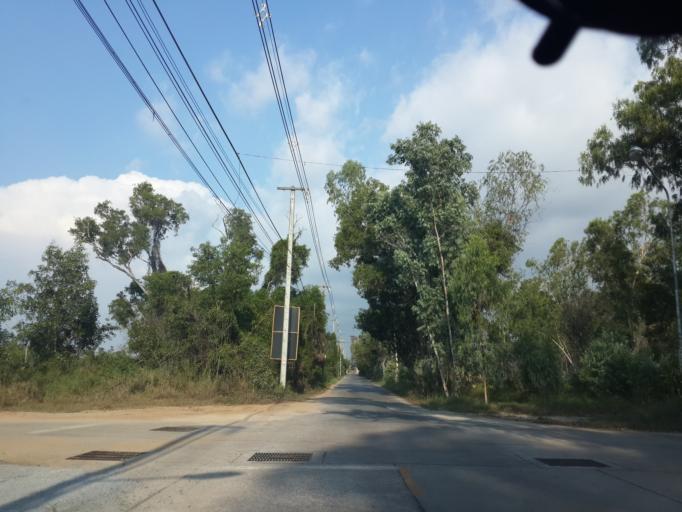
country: TH
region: Chon Buri
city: Phatthaya
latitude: 12.8497
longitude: 100.9049
